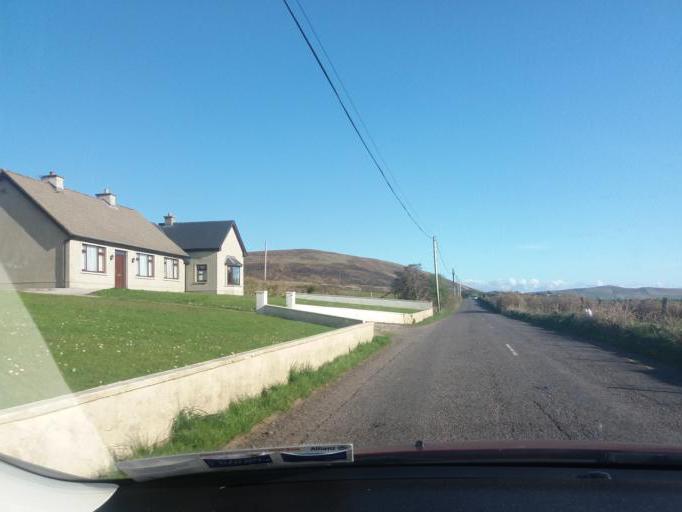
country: IE
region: Munster
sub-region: Ciarrai
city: Dingle
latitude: 52.1654
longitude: -10.2880
